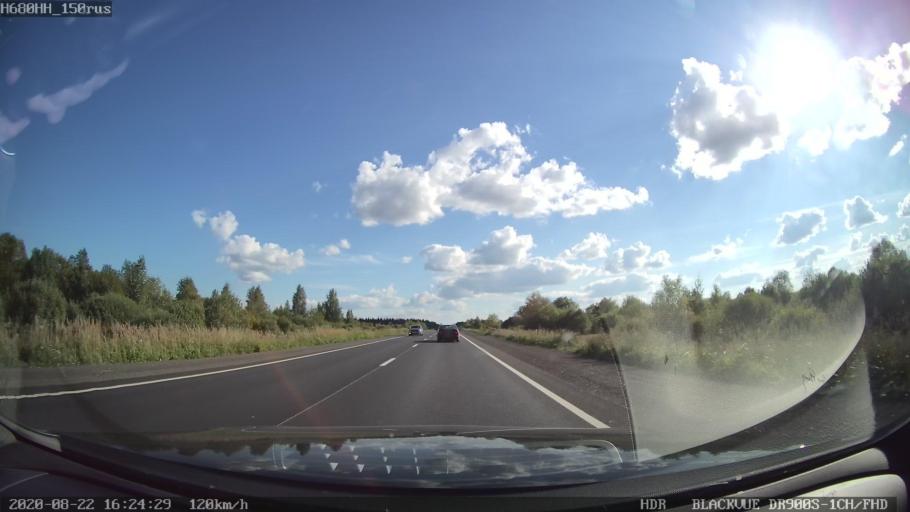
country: RU
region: Tverskaya
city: Rameshki
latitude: 57.3364
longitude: 36.0951
